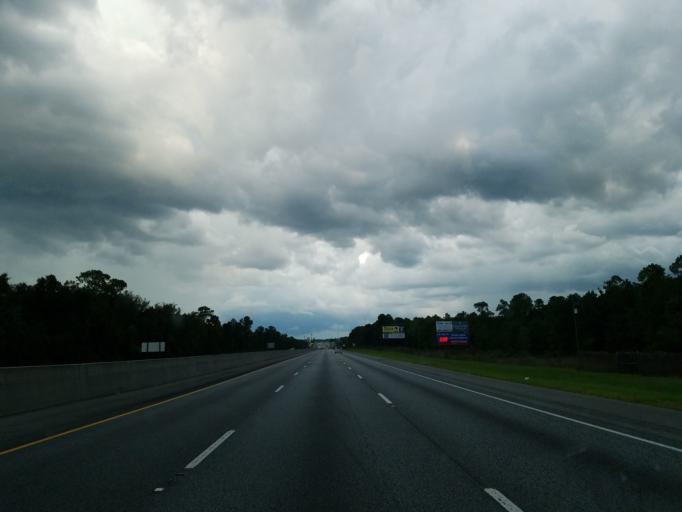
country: US
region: Georgia
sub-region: Lowndes County
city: Remerton
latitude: 30.8664
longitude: -83.3385
